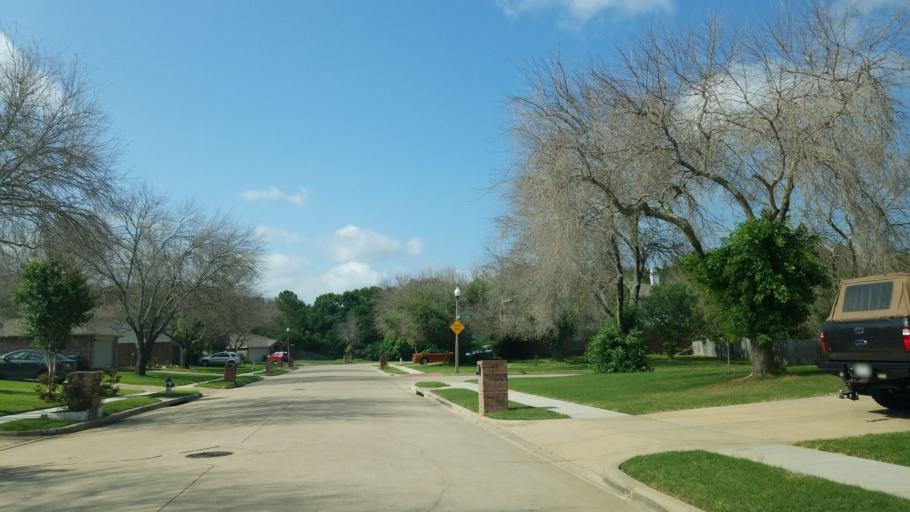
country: US
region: Texas
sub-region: Denton County
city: Copper Canyon
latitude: 33.1366
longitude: -97.1140
